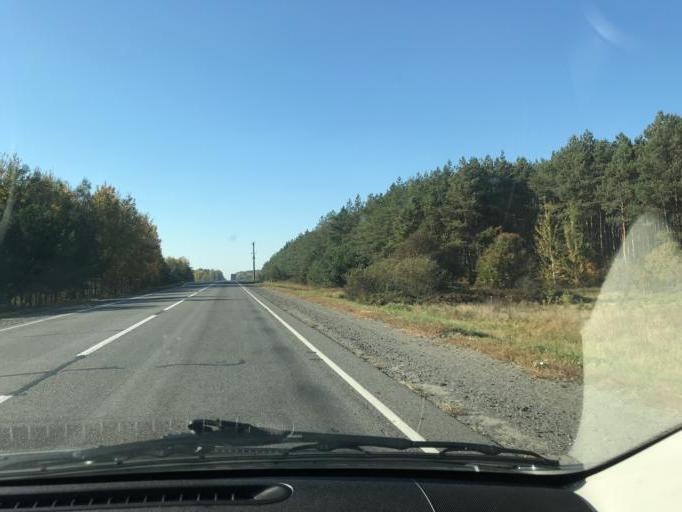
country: BY
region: Brest
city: Davyd-Haradok
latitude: 52.2444
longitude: 27.1468
